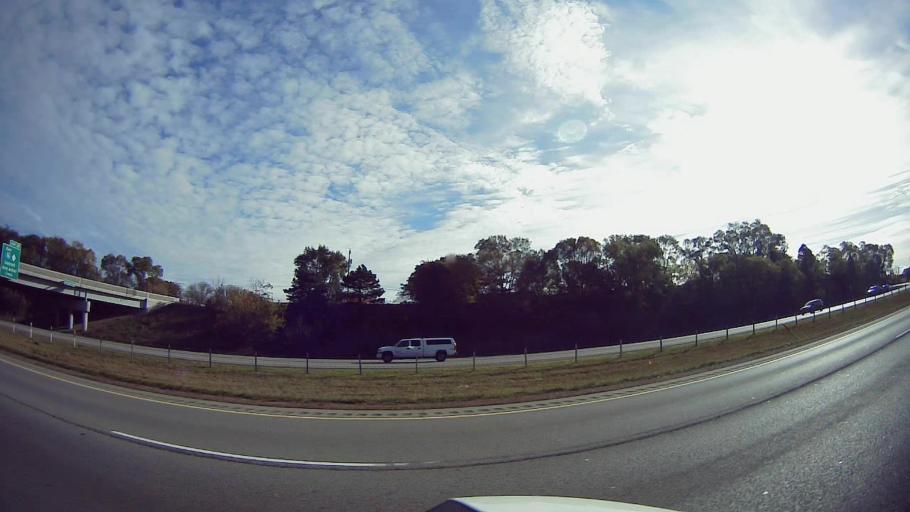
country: US
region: Michigan
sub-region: Wayne County
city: Plymouth
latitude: 42.3608
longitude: -83.4362
